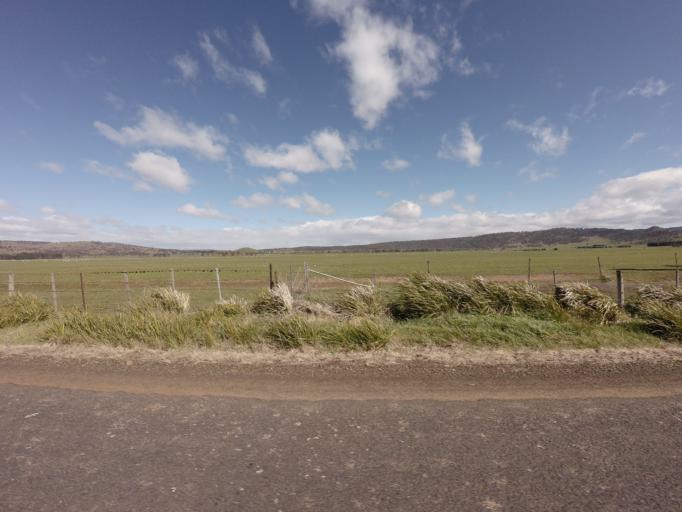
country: AU
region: Tasmania
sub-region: Northern Midlands
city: Evandale
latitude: -42.0145
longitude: 147.4618
